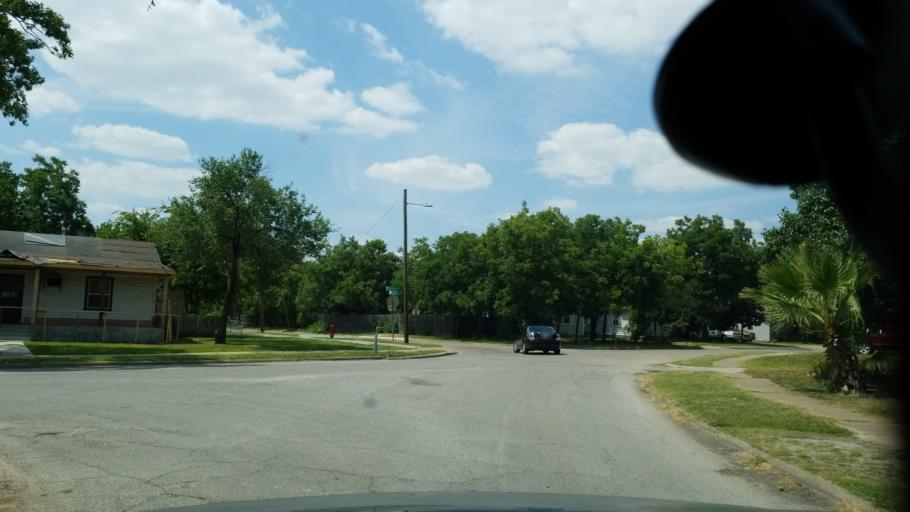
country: US
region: Texas
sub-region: Dallas County
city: Grand Prairie
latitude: 32.7532
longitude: -96.9810
